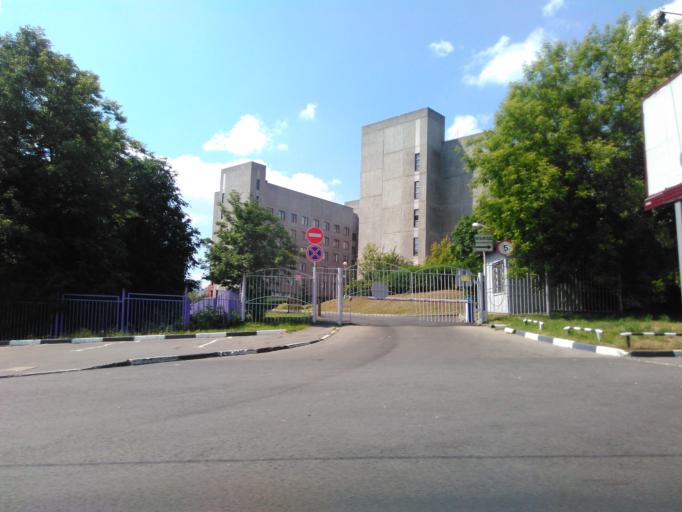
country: RU
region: Moscow
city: Zyuzino
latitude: 55.6676
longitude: 37.5825
